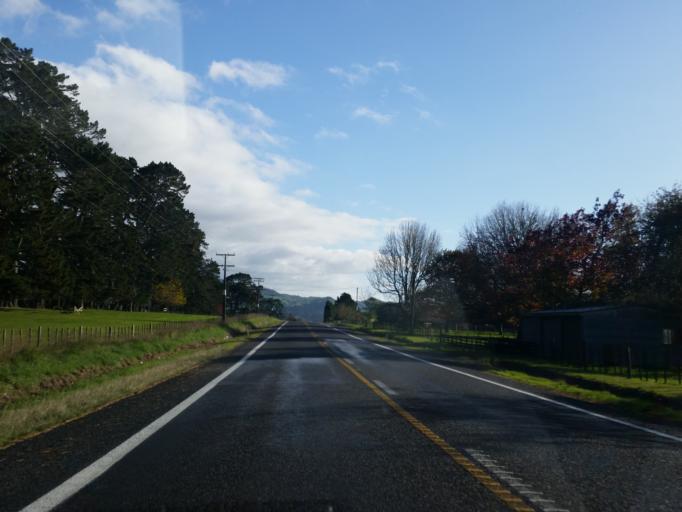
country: NZ
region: Waikato
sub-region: Hauraki District
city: Waihi
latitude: -37.4203
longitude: 175.8675
